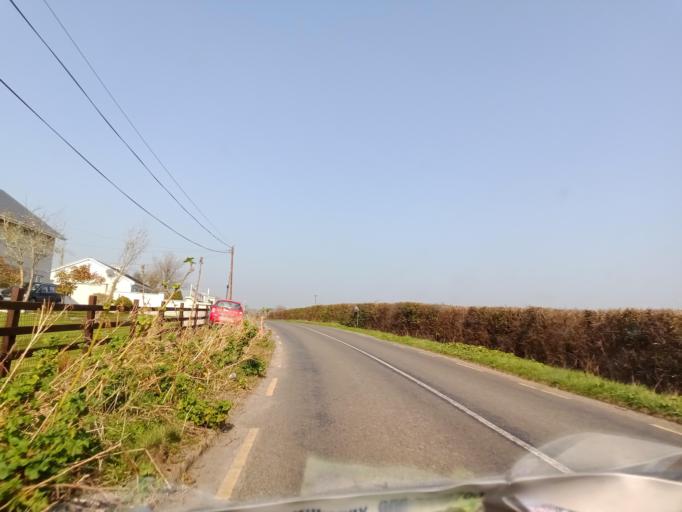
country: IE
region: Leinster
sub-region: Kilkenny
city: Callan
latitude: 52.5306
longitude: -7.3833
